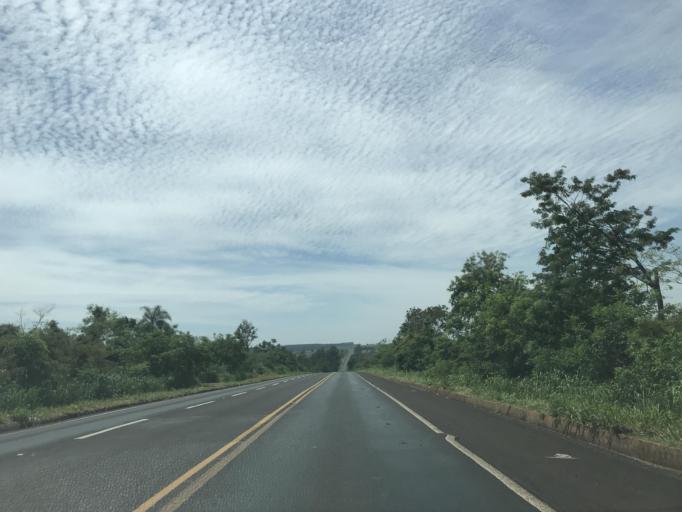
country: BR
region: Parana
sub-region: Paranavai
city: Nova Aurora
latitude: -22.9970
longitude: -52.5782
